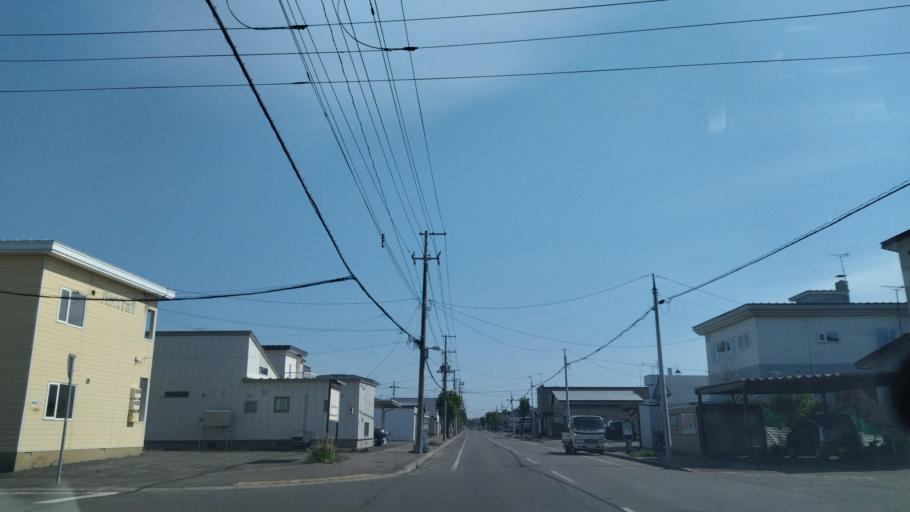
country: JP
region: Hokkaido
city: Obihiro
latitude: 42.9202
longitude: 143.0554
